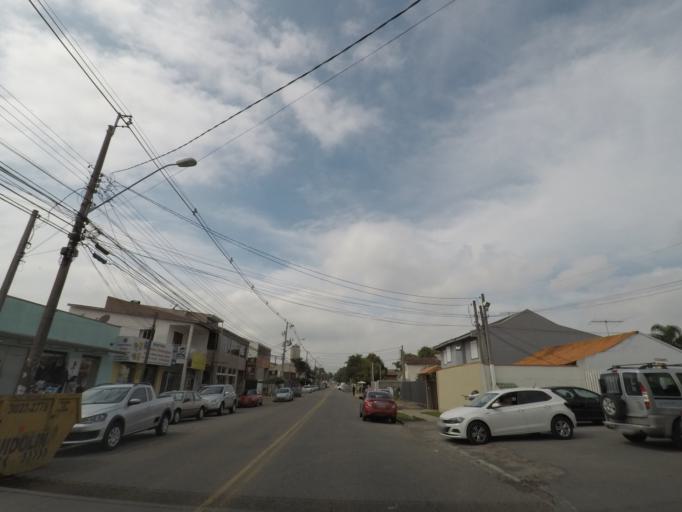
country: BR
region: Parana
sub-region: Curitiba
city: Curitiba
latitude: -25.4890
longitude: -49.3021
